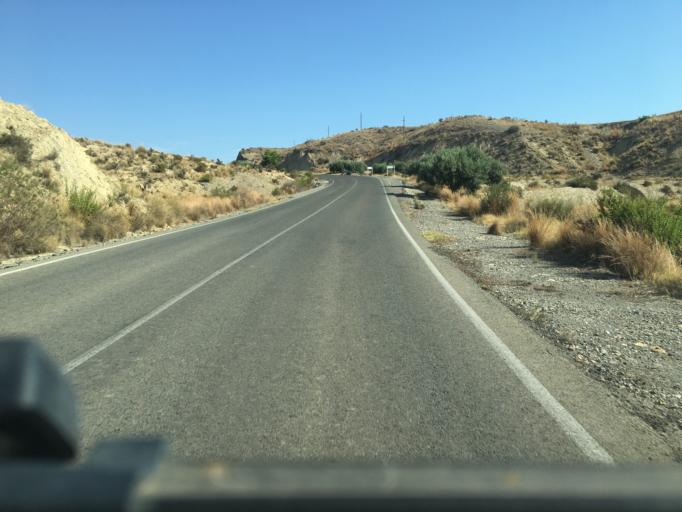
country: ES
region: Andalusia
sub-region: Provincia de Almeria
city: Huercal-Overa
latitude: 37.4295
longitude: -1.9725
